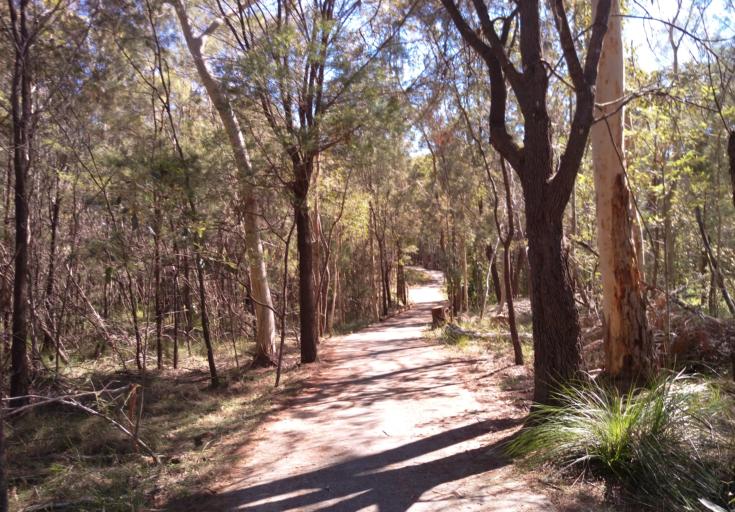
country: AU
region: Queensland
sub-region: Brisbane
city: Burbank
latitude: -27.5524
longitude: 153.2066
